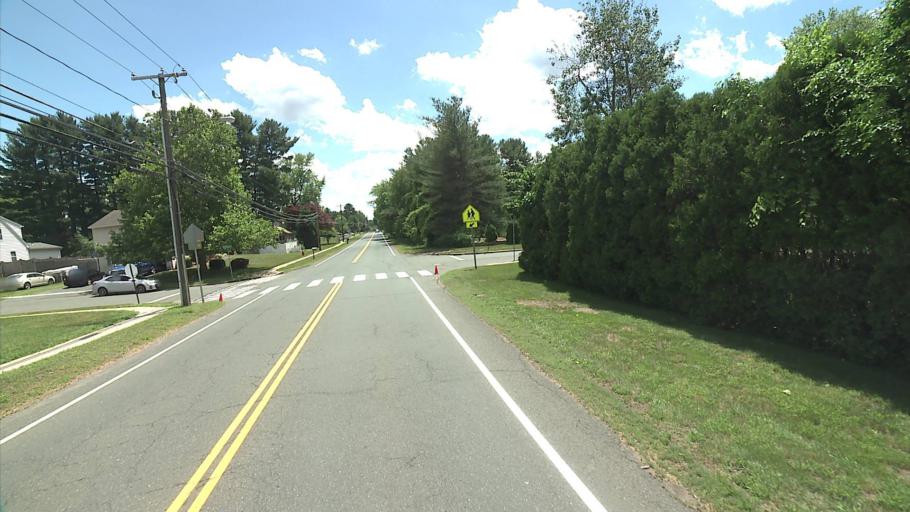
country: US
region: Connecticut
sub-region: Hartford County
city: Hazardville
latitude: 41.9955
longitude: -72.5402
